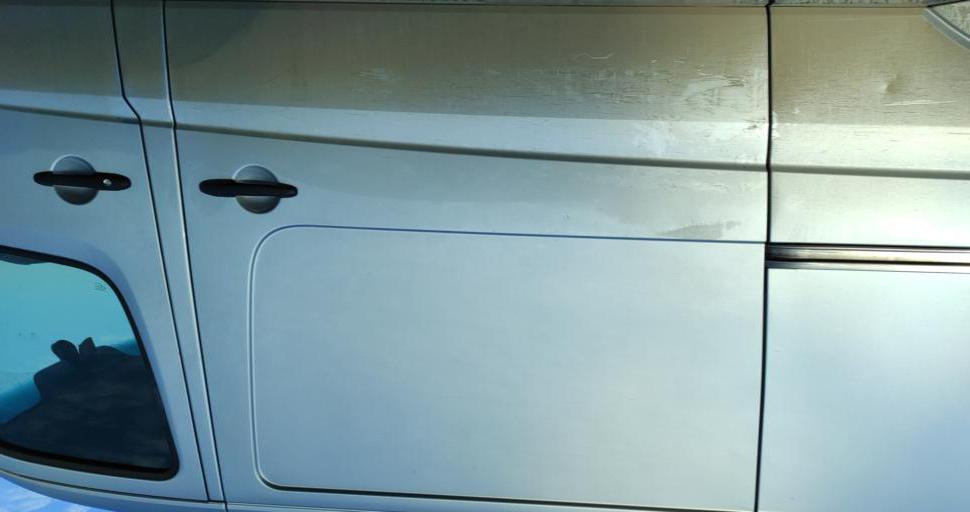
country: AL
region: Durres
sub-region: Rrethi i Krujes
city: Fushe-Kruje
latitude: 41.4901
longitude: 19.7241
